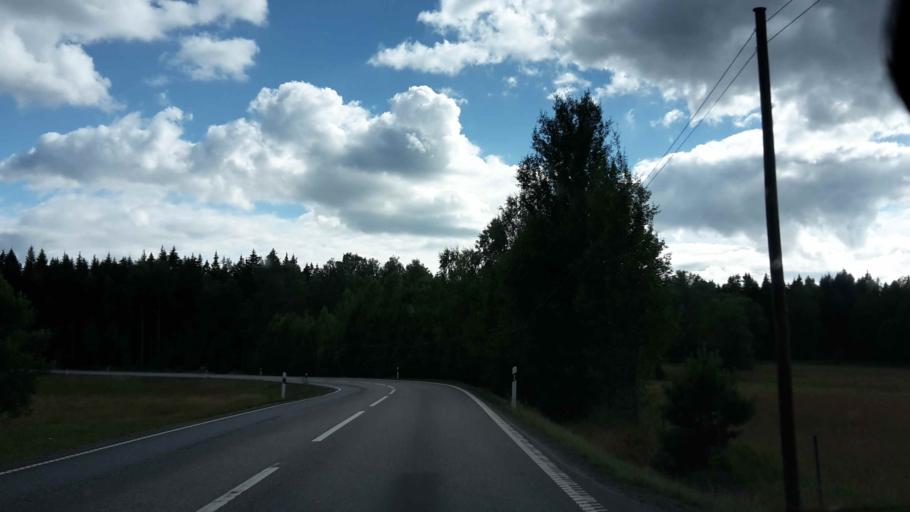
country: SE
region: OErebro
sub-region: Hallsbergs Kommun
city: Palsboda
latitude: 58.8301
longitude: 15.4078
